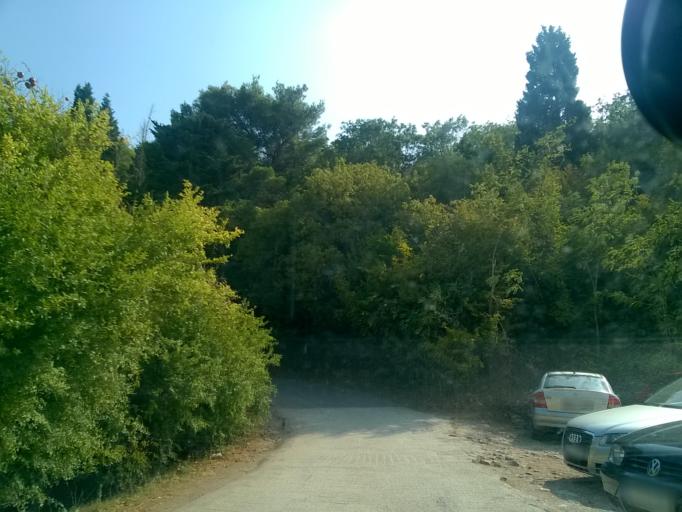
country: ME
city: Petrovac na Moru
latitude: 42.2025
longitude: 18.9490
